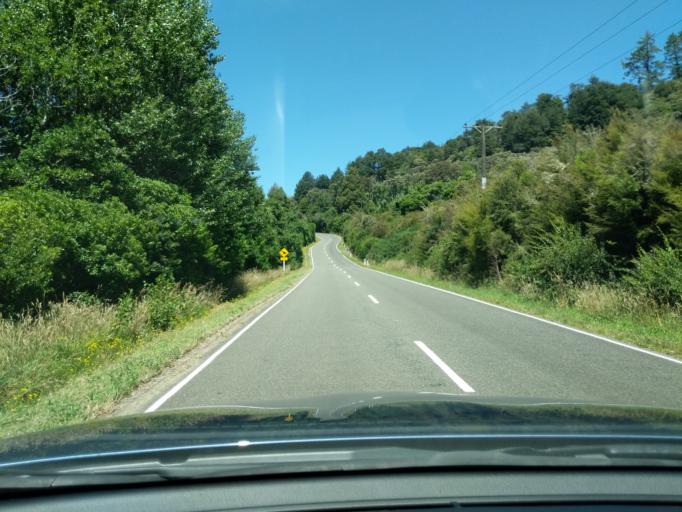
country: NZ
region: Tasman
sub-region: Tasman District
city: Takaka
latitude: -40.7240
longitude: 172.6027
